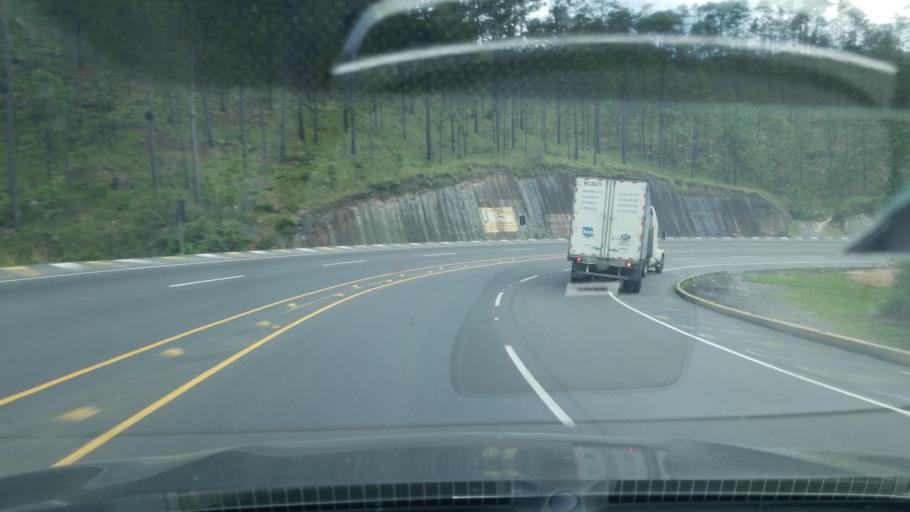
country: HN
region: Francisco Morazan
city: Zambrano
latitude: 14.2848
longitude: -87.4554
